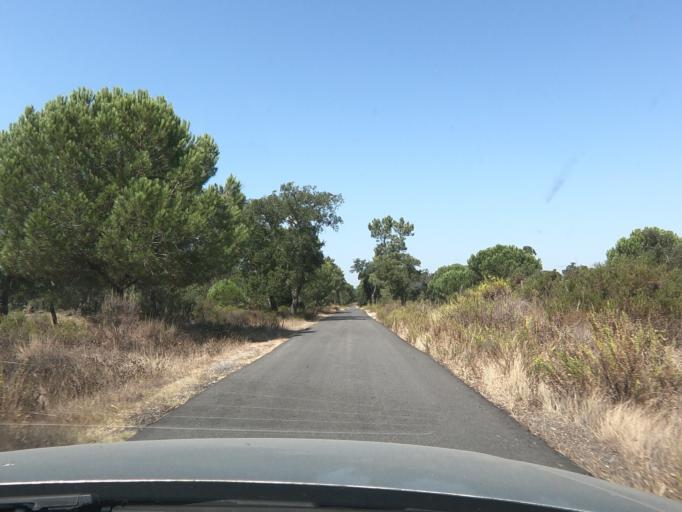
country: PT
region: Setubal
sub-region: Alcacer do Sal
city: Alcacer do Sal
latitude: 38.2638
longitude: -8.3126
